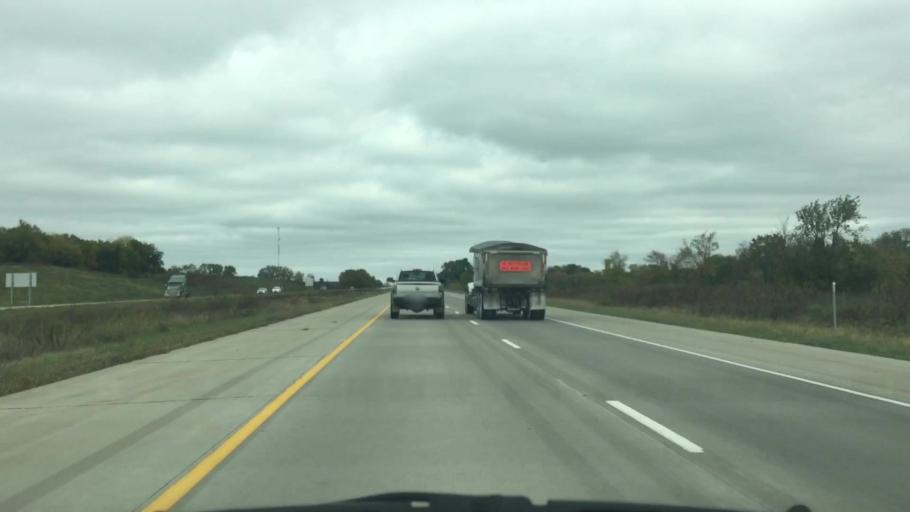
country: US
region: Iowa
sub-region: Warren County
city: Norwalk
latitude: 41.3776
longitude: -93.7802
